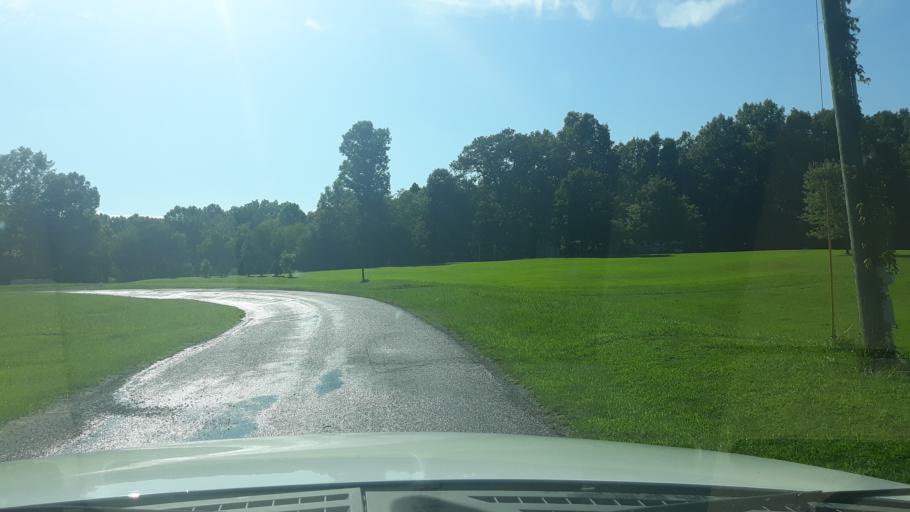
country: US
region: Illinois
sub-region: Saline County
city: Harrisburg
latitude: 37.8557
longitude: -88.5848
